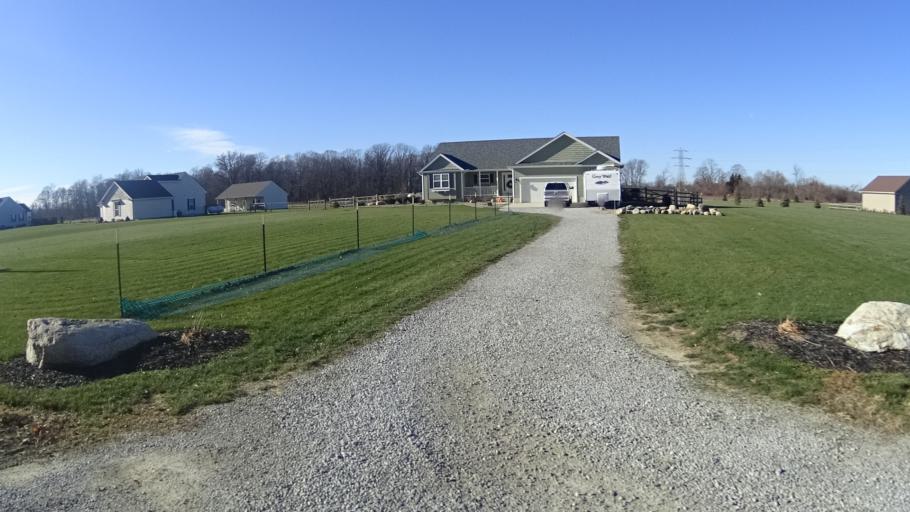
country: US
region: Ohio
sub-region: Lorain County
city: Vermilion-on-the-Lake
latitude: 41.3725
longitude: -82.3197
